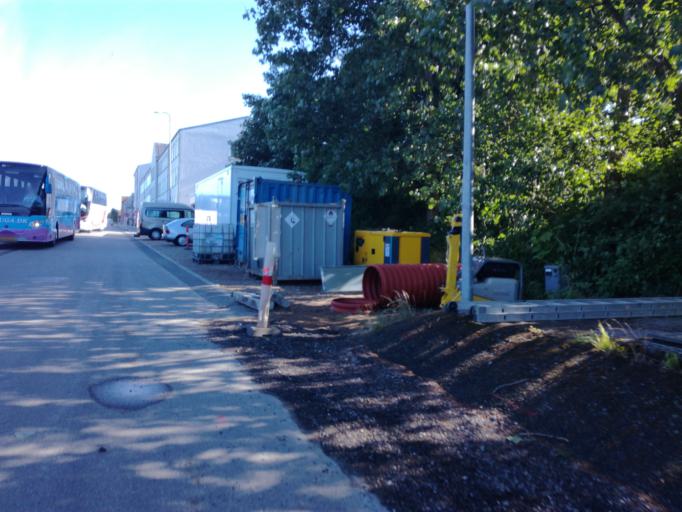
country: DK
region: South Denmark
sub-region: Fredericia Kommune
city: Fredericia
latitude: 55.5589
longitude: 9.7637
